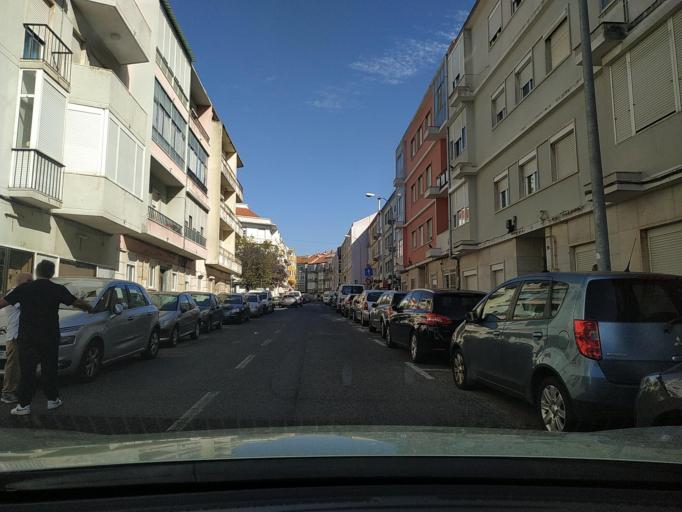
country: PT
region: Lisbon
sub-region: Sintra
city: Queluz
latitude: 38.7594
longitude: -9.2432
